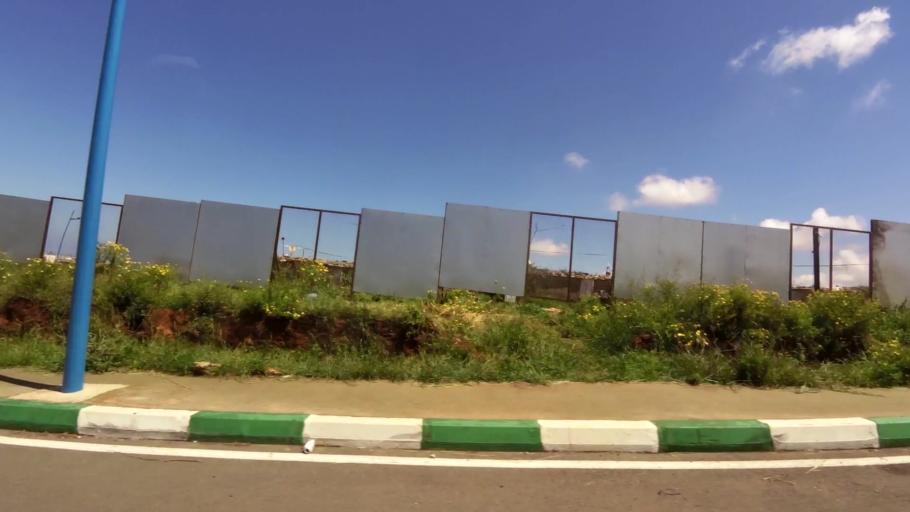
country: MA
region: Grand Casablanca
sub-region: Nouaceur
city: Dar Bouazza
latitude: 33.5231
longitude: -7.7790
